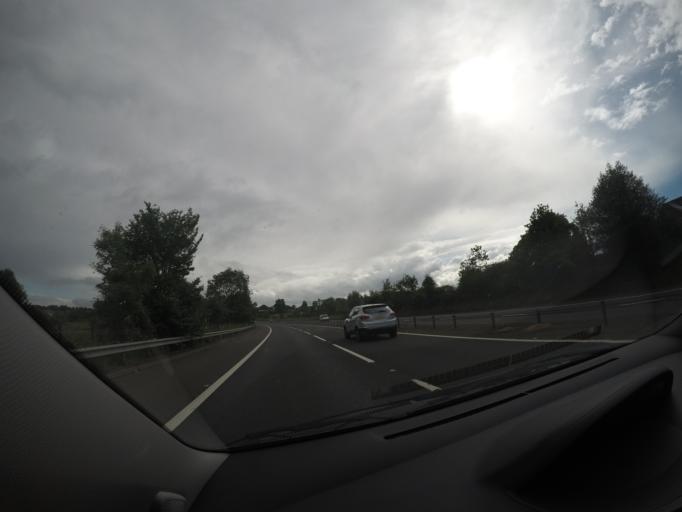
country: GB
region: Scotland
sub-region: Falkirk
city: Dunipace
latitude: 56.0340
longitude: -3.9226
